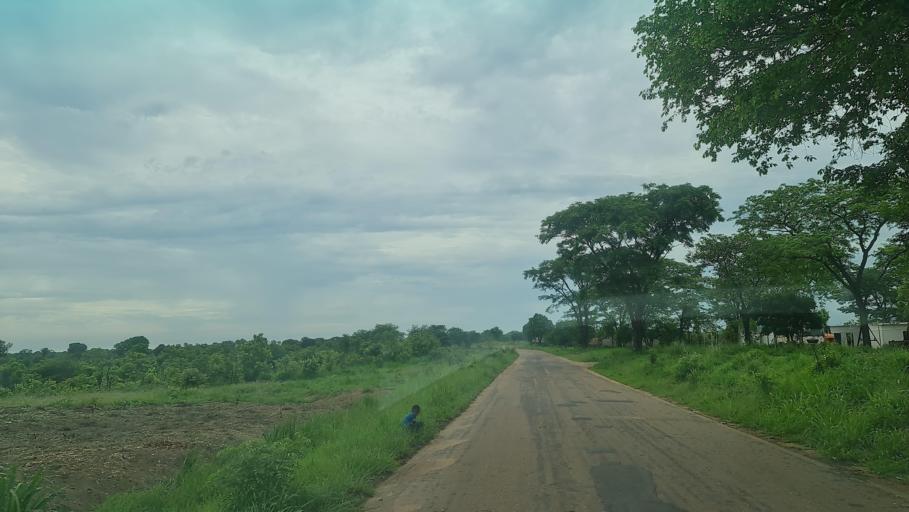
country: MW
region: Southern Region
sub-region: Nsanje District
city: Nsanje
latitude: -17.6907
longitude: 35.7340
